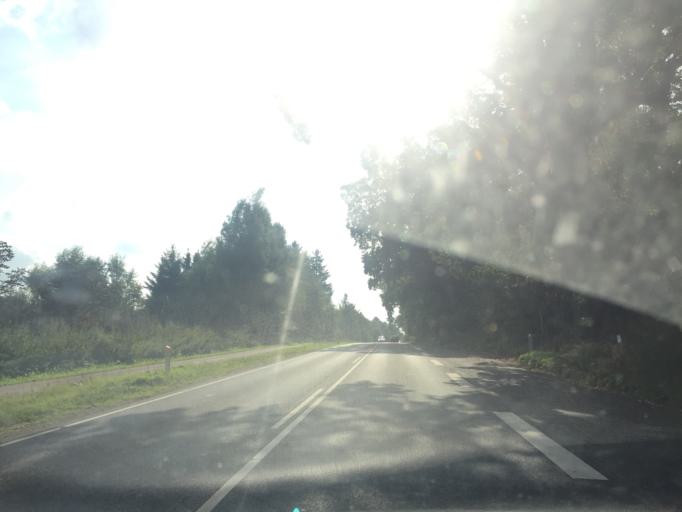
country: DK
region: Zealand
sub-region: Lejre Kommune
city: Ejby
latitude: 55.6666
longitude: 11.8260
